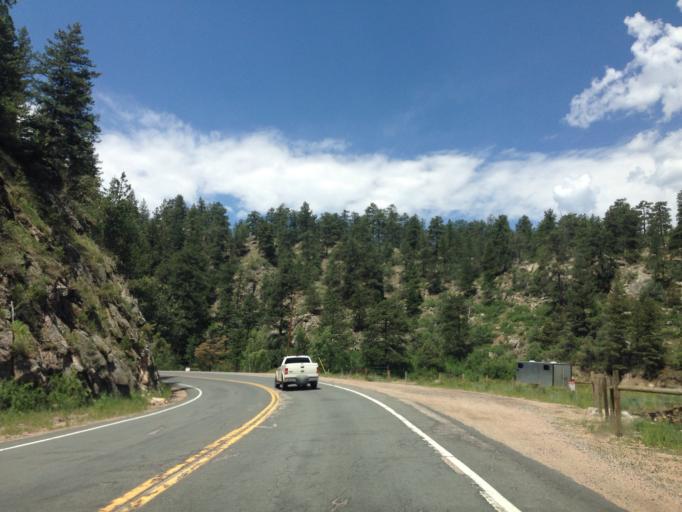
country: US
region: Colorado
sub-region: Larimer County
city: Estes Park
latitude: 40.3944
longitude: -105.4232
